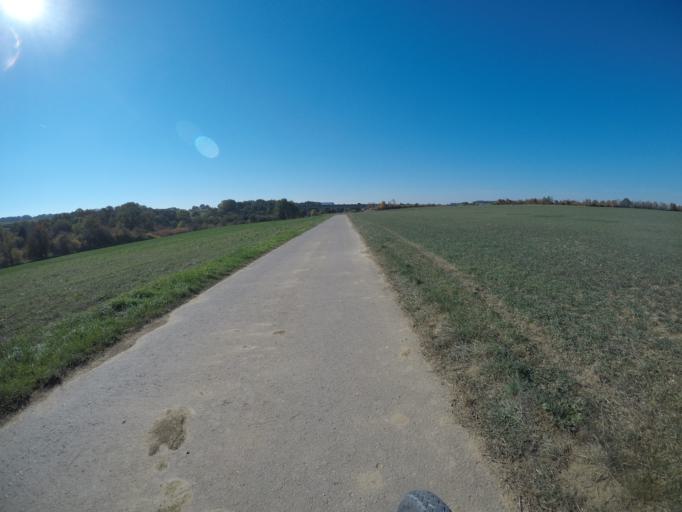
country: DE
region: Baden-Wuerttemberg
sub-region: Regierungsbezirk Stuttgart
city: Bondorf
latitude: 48.5396
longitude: 8.8952
